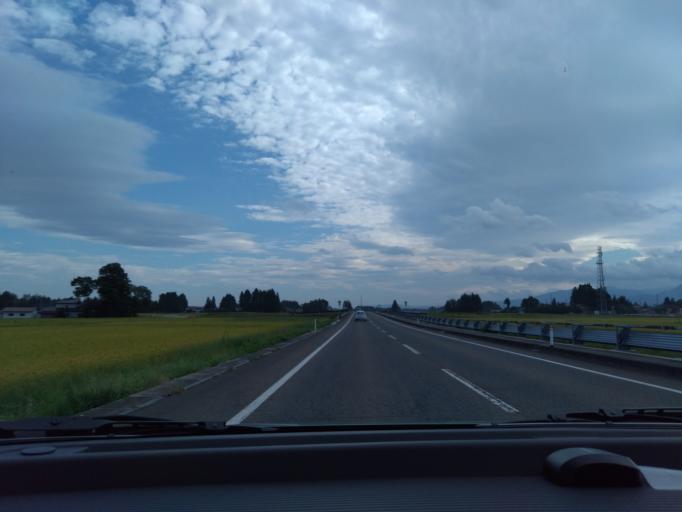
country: JP
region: Iwate
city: Hanamaki
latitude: 39.3541
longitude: 141.0541
